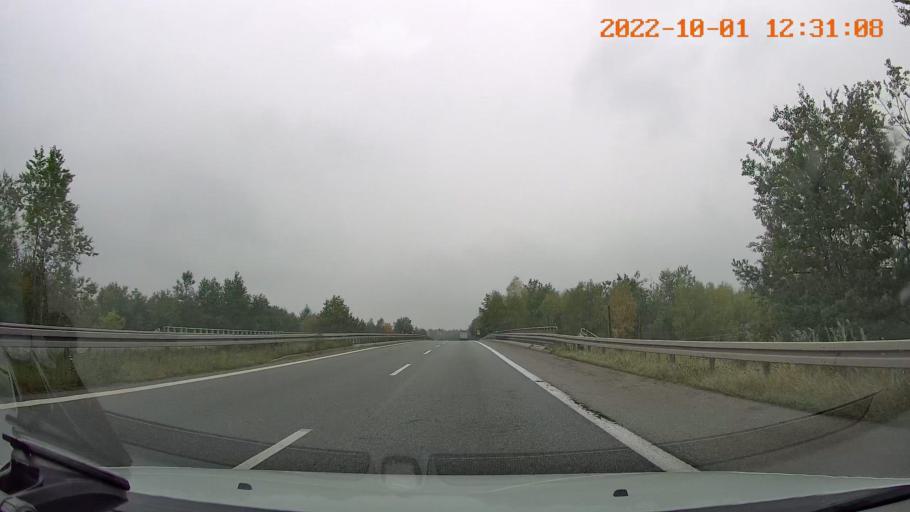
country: PL
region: Silesian Voivodeship
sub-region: Powiat bierunsko-ledzinski
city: Imielin
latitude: 50.1687
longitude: 19.1640
